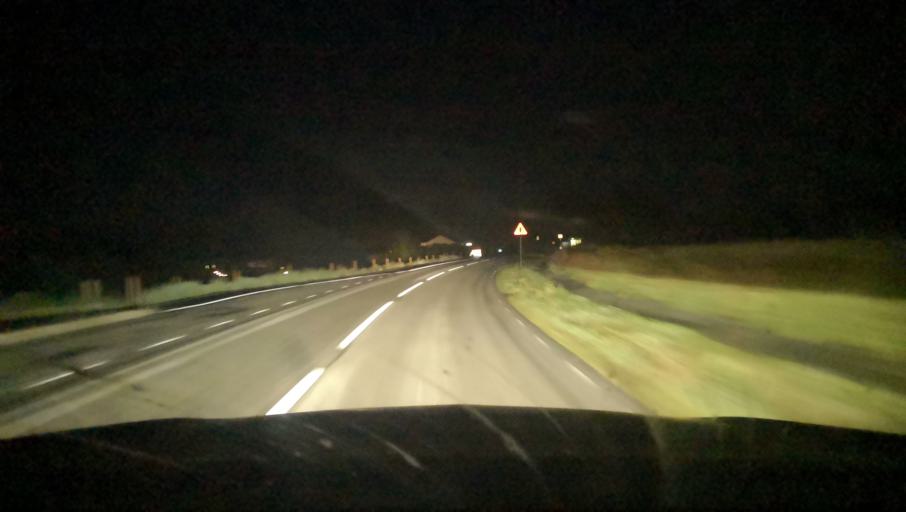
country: SE
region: Skane
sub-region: Simrishamns Kommun
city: Kivik
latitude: 55.7154
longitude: 14.1527
